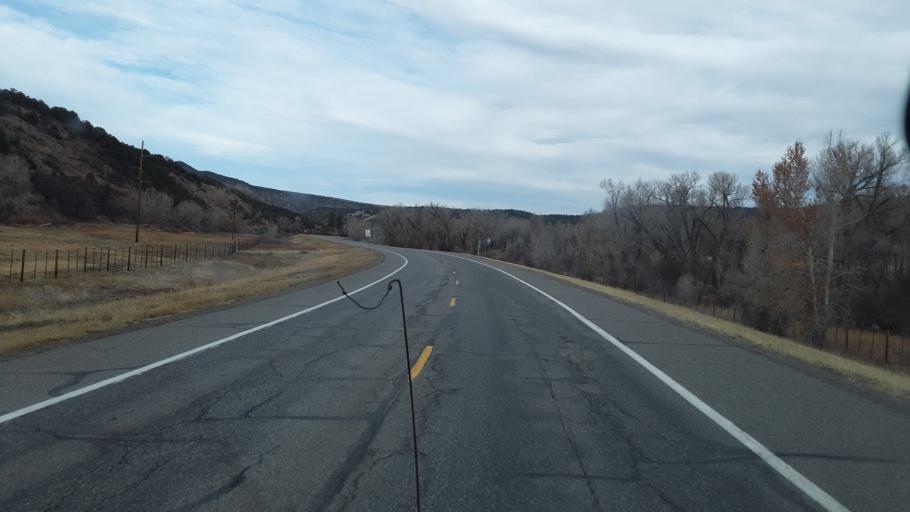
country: US
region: Colorado
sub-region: Ouray County
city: Ouray
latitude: 38.2311
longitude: -107.7302
